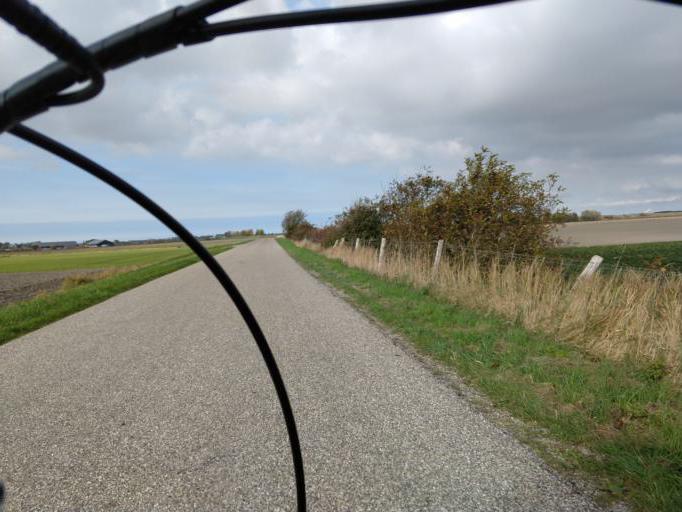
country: NL
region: Zeeland
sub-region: Schouwen-Duiveland
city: Scharendijke
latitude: 51.6914
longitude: 3.9497
